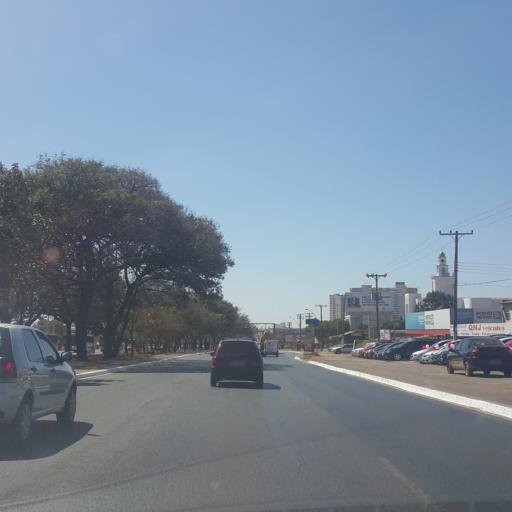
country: BR
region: Federal District
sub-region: Brasilia
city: Brasilia
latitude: -15.8099
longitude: -48.0887
